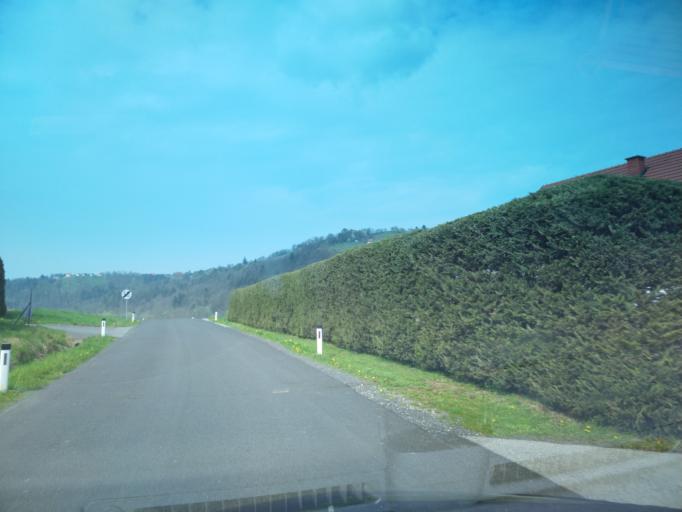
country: AT
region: Styria
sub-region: Politischer Bezirk Leibnitz
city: Kitzeck im Sausal
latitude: 46.7533
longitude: 15.4182
